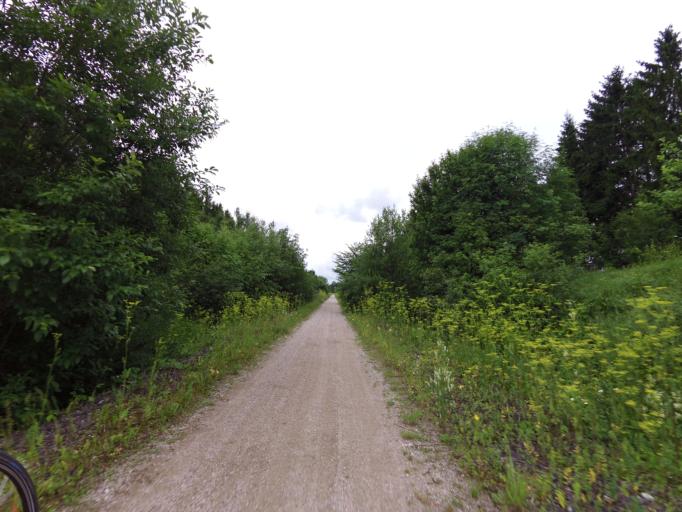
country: EE
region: Harju
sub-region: Nissi vald
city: Turba
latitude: 59.0012
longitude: 24.0618
